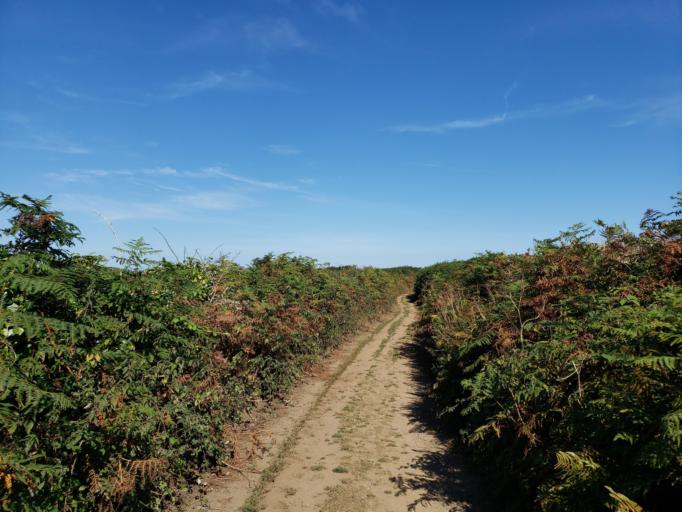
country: GB
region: England
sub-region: Cornwall
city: St Ives
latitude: 50.2102
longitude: -5.5012
